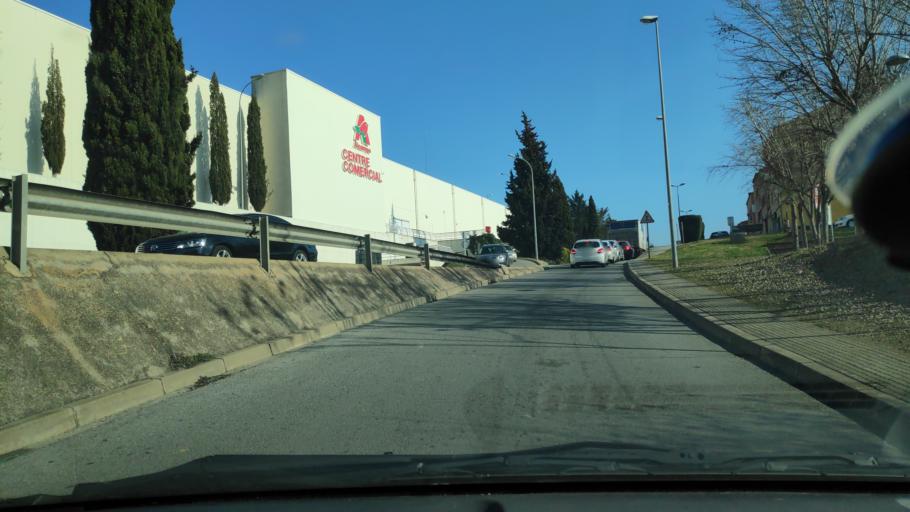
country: ES
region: Catalonia
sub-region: Provincia de Barcelona
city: Sant Quirze del Valles
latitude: 41.5278
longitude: 2.0887
